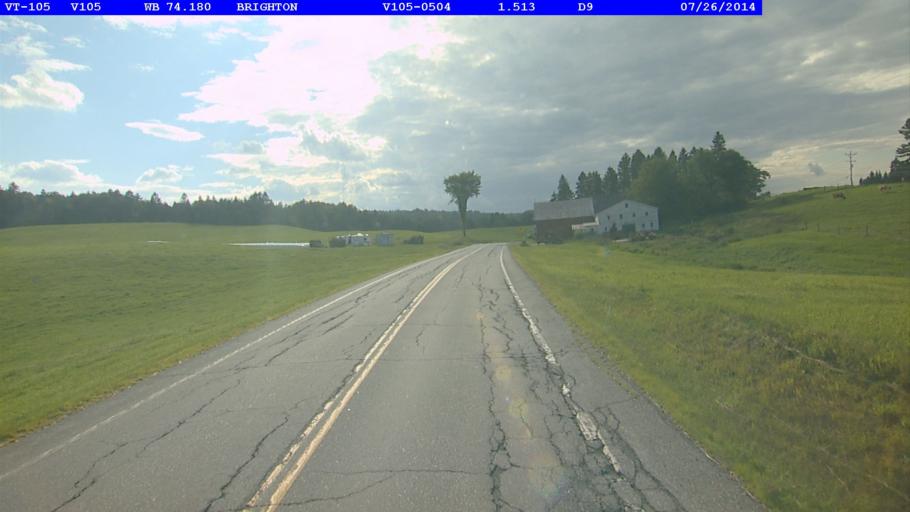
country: US
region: Vermont
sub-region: Caledonia County
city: Lyndonville
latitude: 44.8039
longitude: -71.9201
